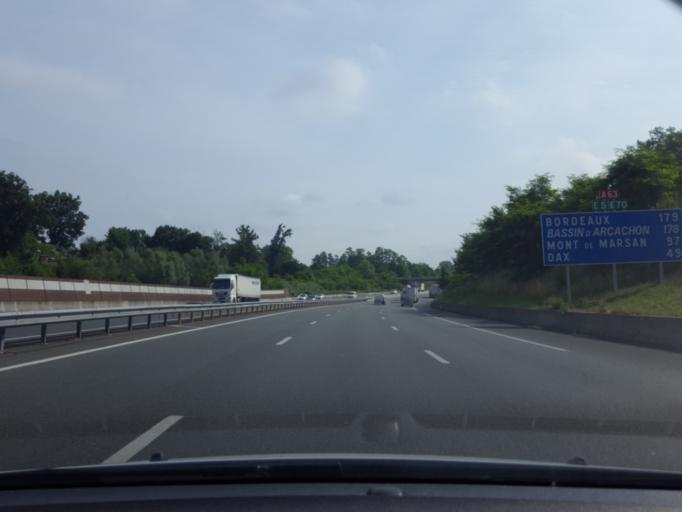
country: FR
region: Aquitaine
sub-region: Departement des Pyrenees-Atlantiques
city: Boucau
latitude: 43.4950
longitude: -1.4480
